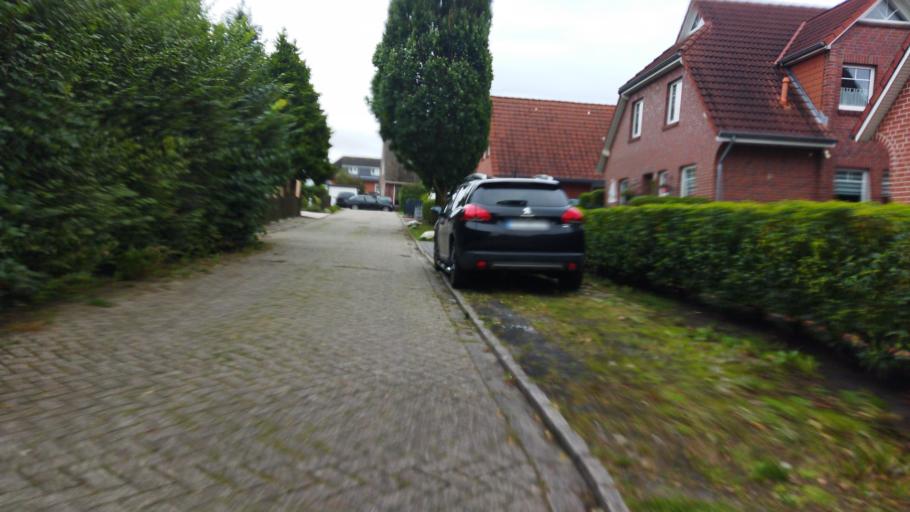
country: DE
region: Lower Saxony
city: Hinte
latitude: 53.4156
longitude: 7.1921
